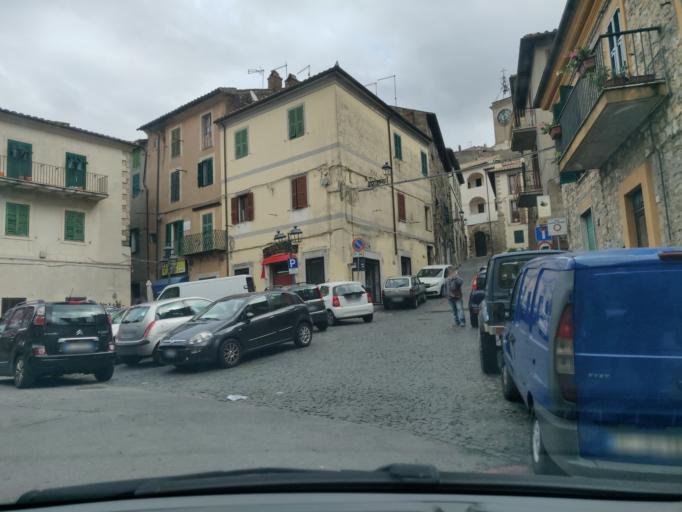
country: IT
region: Latium
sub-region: Citta metropolitana di Roma Capitale
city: Tolfa
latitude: 42.1516
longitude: 11.9400
